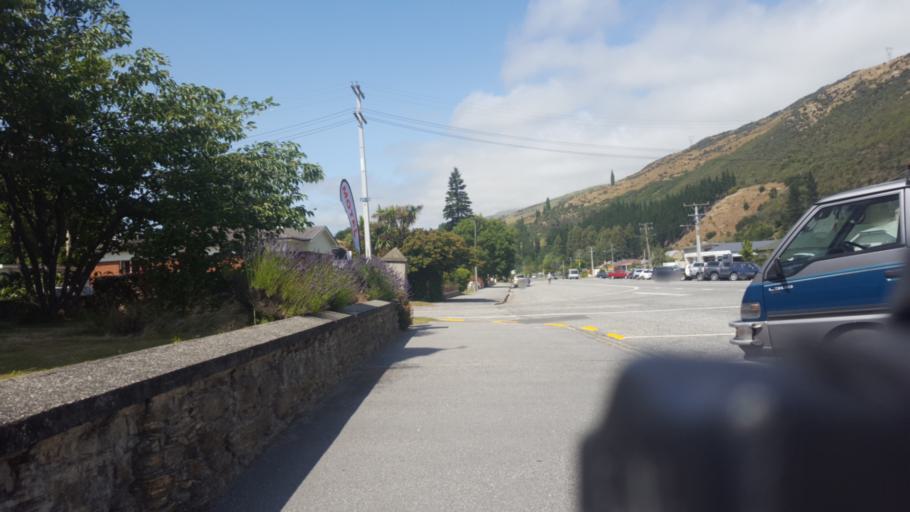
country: NZ
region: Otago
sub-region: Queenstown-Lakes District
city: Kingston
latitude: -45.5427
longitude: 169.3151
